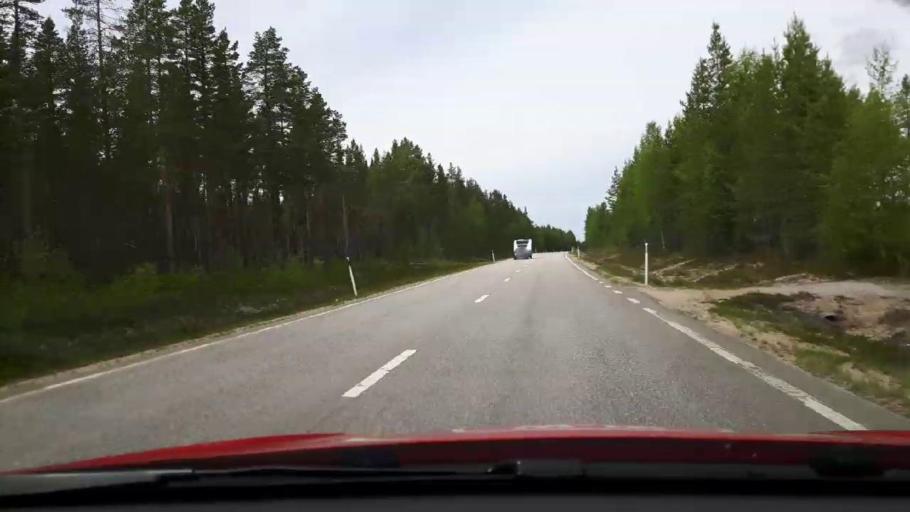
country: SE
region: Jaemtland
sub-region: Harjedalens Kommun
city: Sveg
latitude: 62.1121
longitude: 14.1837
